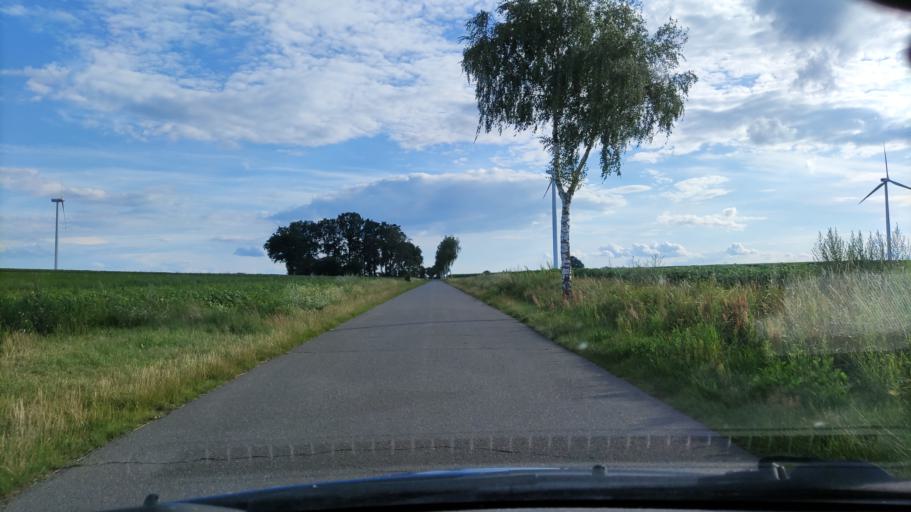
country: DE
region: Lower Saxony
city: Boitze
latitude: 53.1593
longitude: 10.7572
